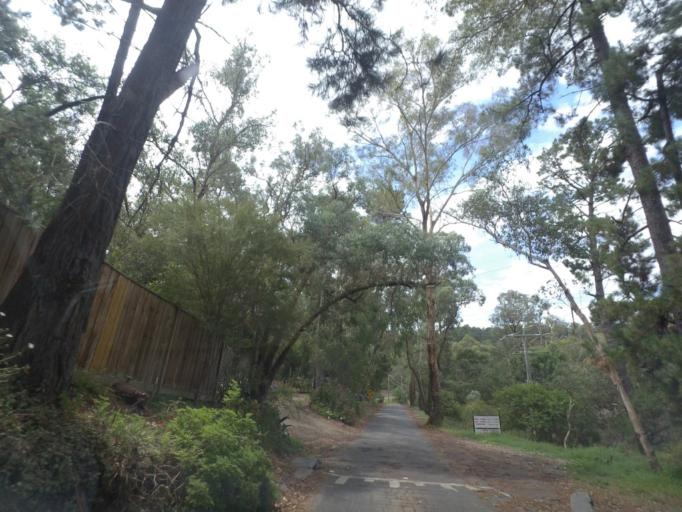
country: AU
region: Victoria
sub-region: Manningham
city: Park Orchards
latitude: -37.7934
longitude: 145.2085
